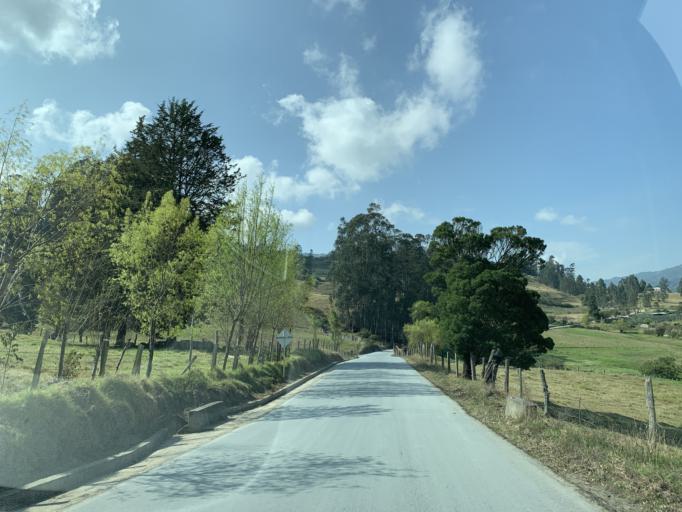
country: CO
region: Boyaca
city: Turmeque
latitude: 5.3141
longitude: -73.4952
